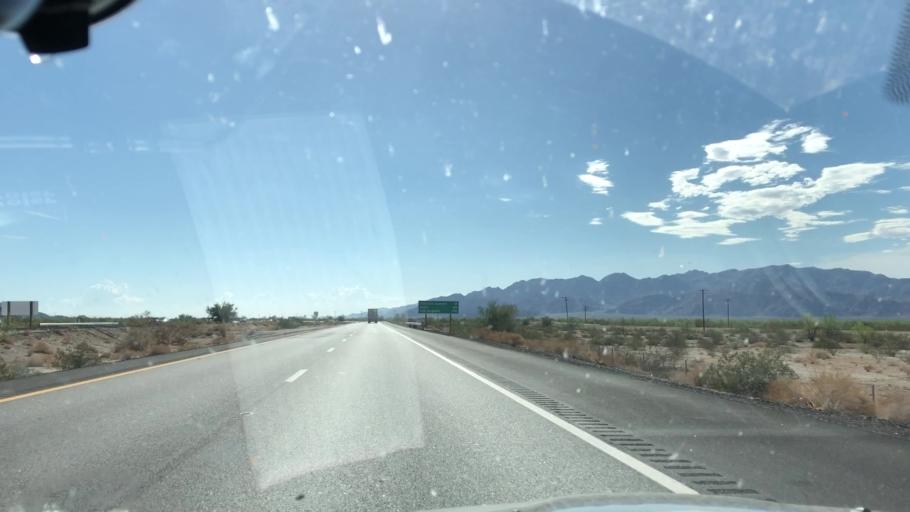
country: US
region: California
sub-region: Imperial County
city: Niland
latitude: 33.7106
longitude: -115.4103
